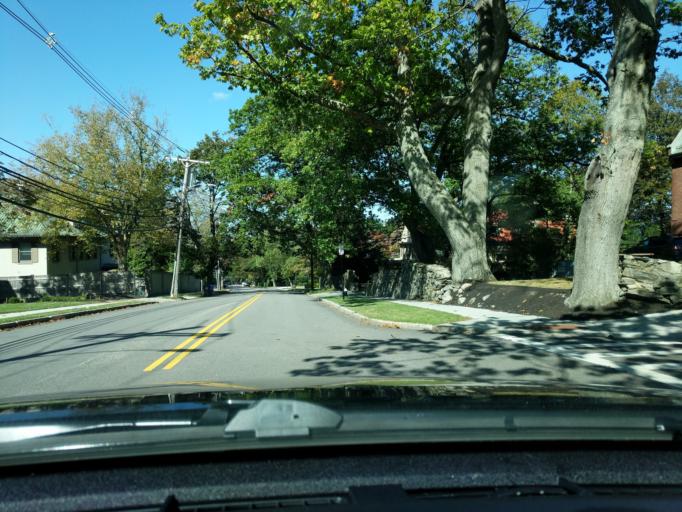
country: US
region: Massachusetts
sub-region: Norfolk County
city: Brookline
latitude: 42.3314
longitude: -71.1434
